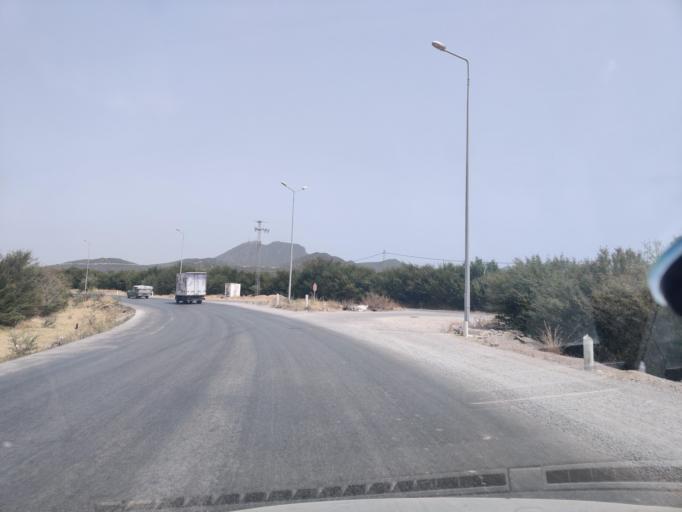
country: TN
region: Tunis
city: La Sebala du Mornag
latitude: 36.6658
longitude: 10.3252
